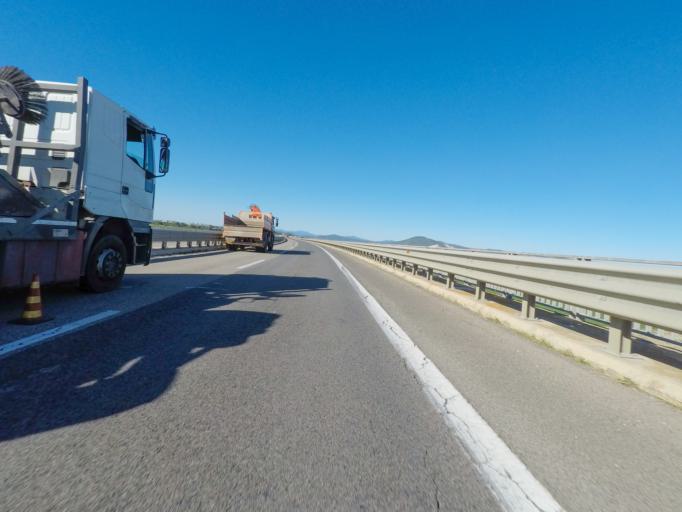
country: IT
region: Tuscany
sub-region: Provincia di Grosseto
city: Grosseto
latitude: 42.7518
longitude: 11.1429
